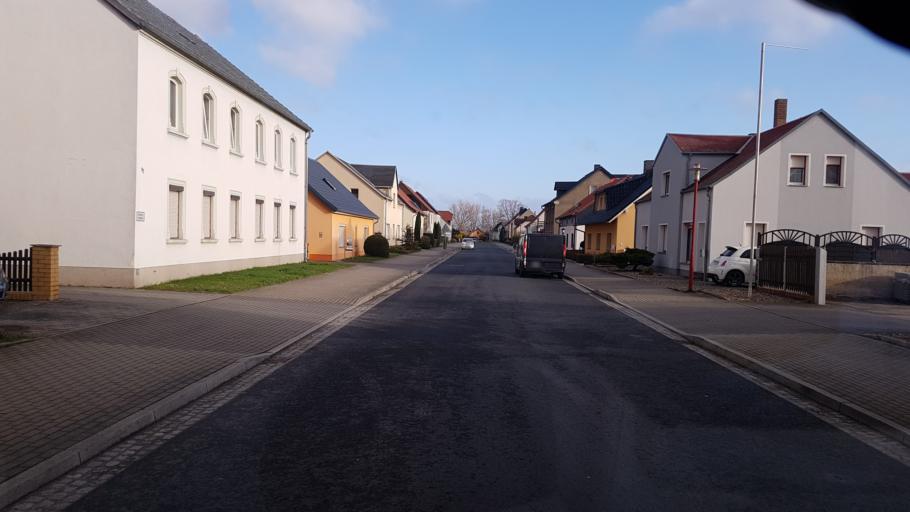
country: DE
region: Saxony
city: Nauwalde
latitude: 51.4171
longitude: 13.4448
